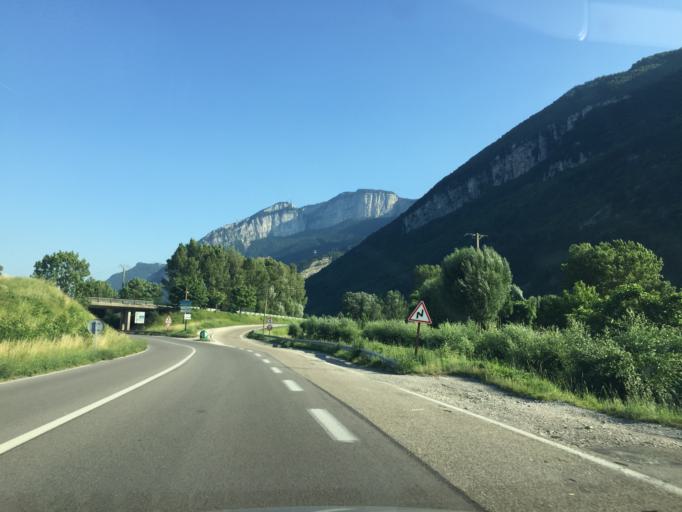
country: FR
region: Rhone-Alpes
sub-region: Departement de l'Isere
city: Veurey-Voroize
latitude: 45.2719
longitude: 5.6191
